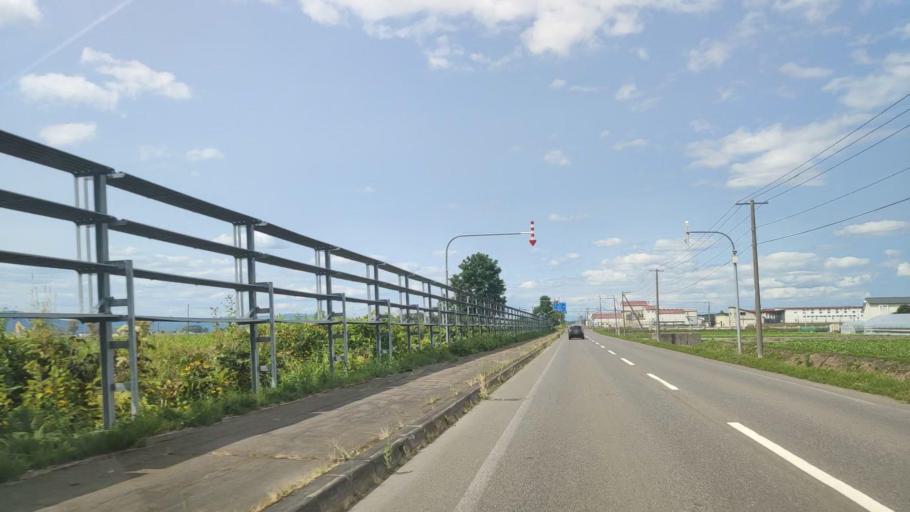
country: JP
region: Hokkaido
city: Nayoro
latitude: 44.1988
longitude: 142.4158
